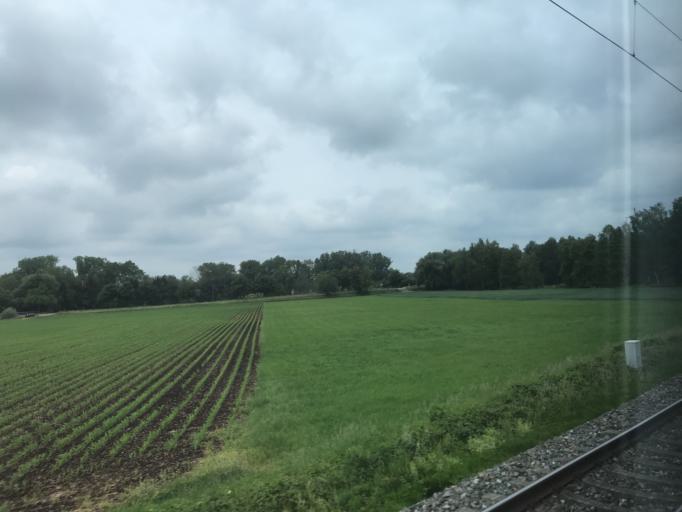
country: DE
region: Bavaria
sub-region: Swabia
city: Burgau
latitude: 48.4525
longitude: 10.4101
